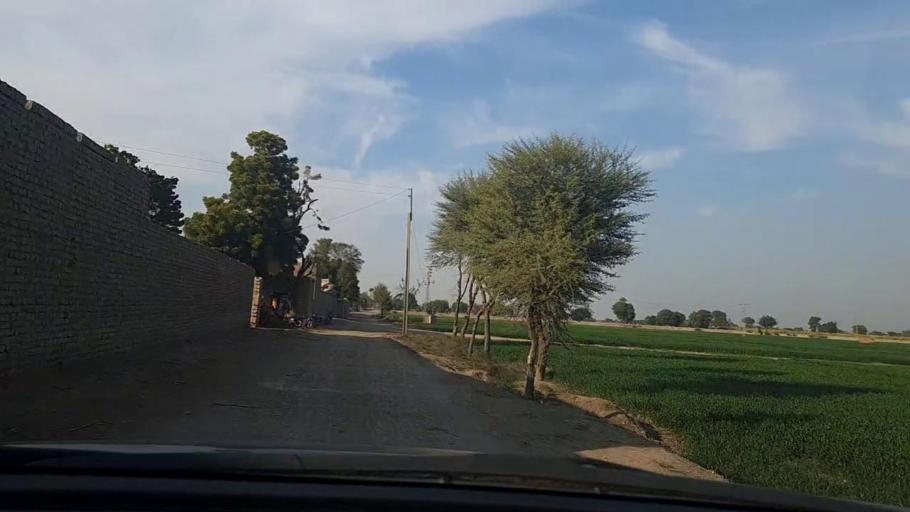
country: PK
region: Sindh
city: Daulatpur
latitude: 26.3182
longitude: 68.0208
